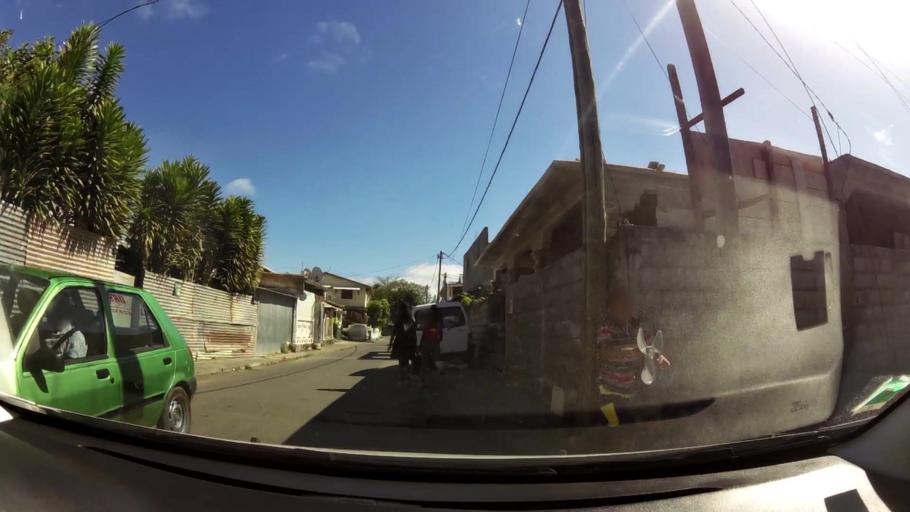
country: YT
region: Pamandzi
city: Pamandzi
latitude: -12.7865
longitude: 45.2758
